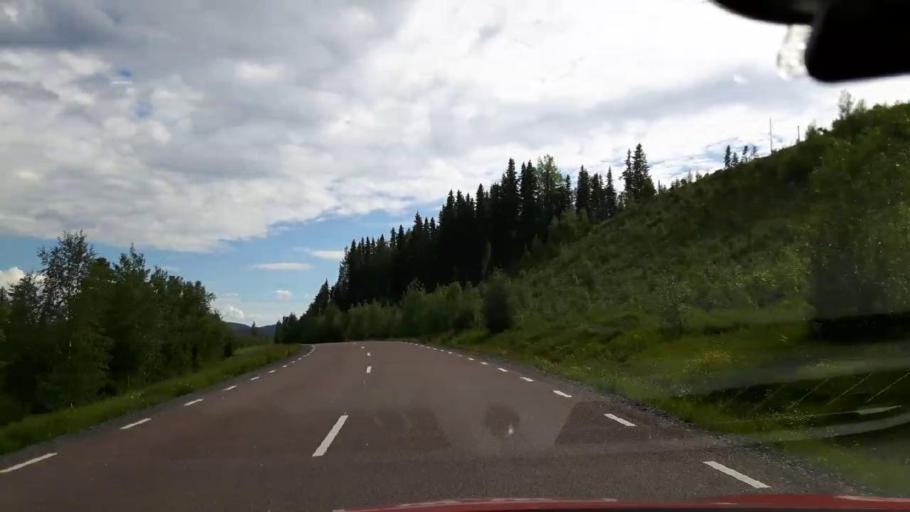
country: SE
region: Jaemtland
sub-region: Krokoms Kommun
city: Valla
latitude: 63.9386
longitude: 14.2211
